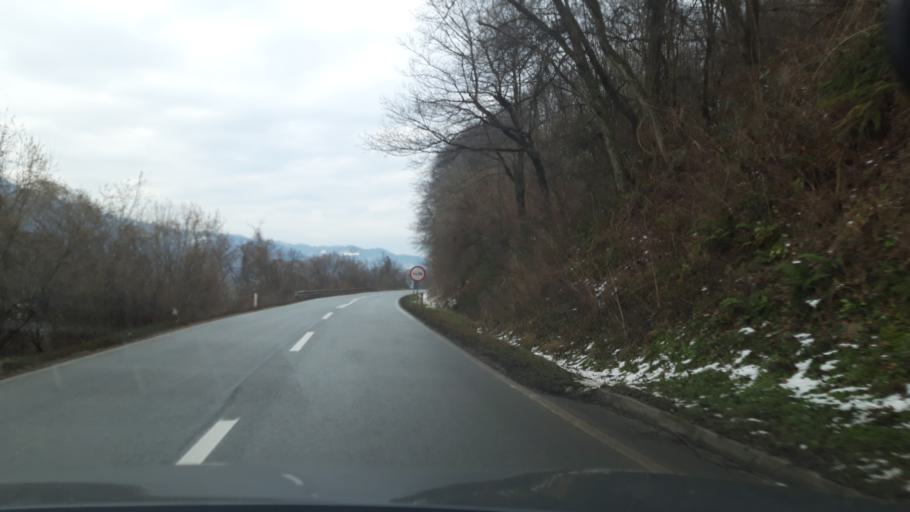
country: RS
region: Central Serbia
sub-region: Macvanski Okrug
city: Mali Zvornik
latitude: 44.3031
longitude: 19.1439
